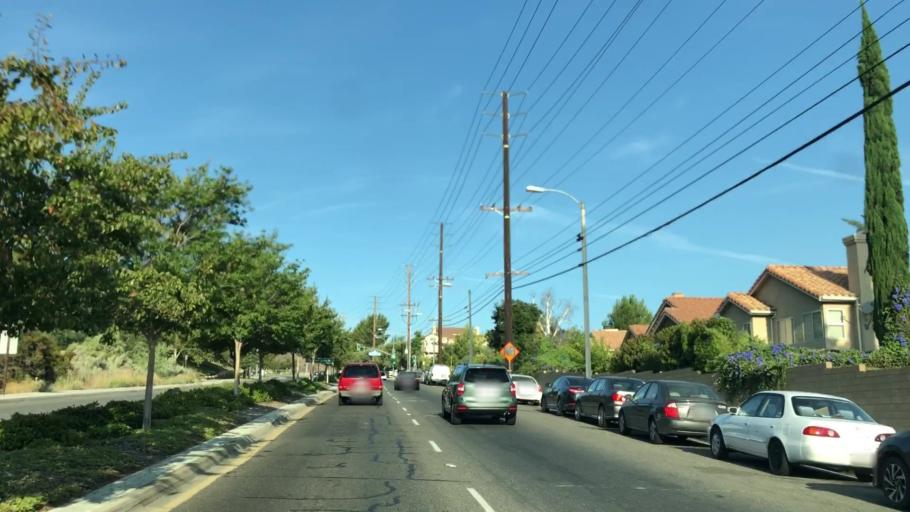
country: US
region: California
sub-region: Los Angeles County
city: Santa Clarita
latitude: 34.3981
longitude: -118.4788
